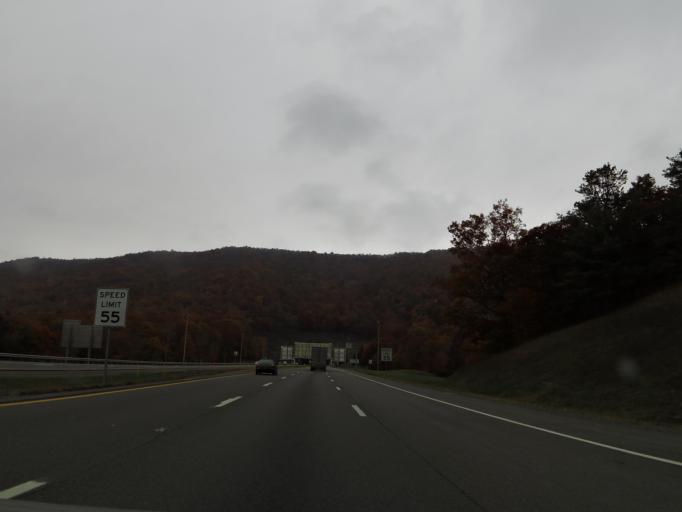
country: US
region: Virginia
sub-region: Bland County
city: Bland
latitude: 37.0326
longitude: -81.1220
